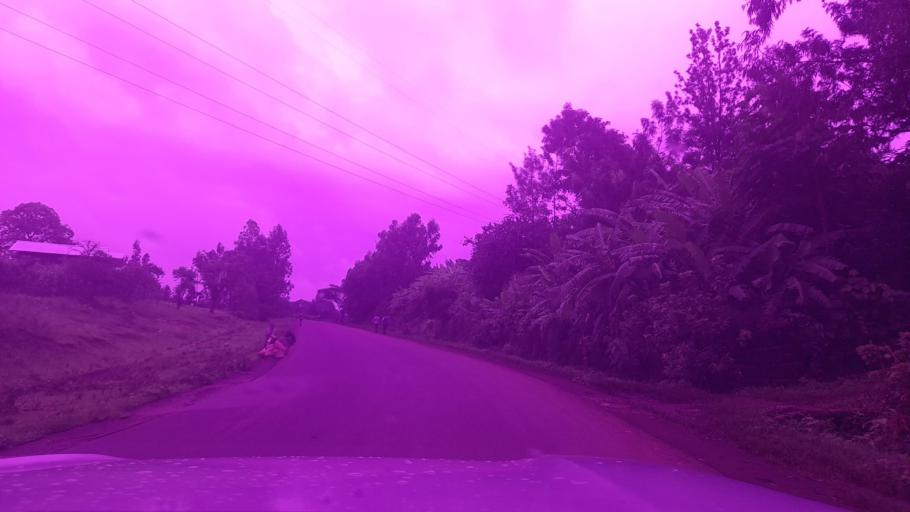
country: ET
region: Oromiya
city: Jima
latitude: 7.7488
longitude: 37.1626
